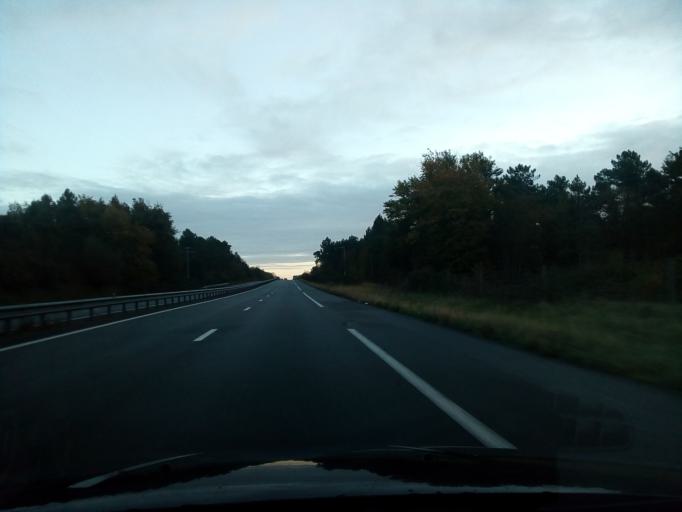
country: FR
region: Poitou-Charentes
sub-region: Departement de la Charente-Maritime
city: Montlieu-la-Garde
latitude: 45.2196
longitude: -0.2887
